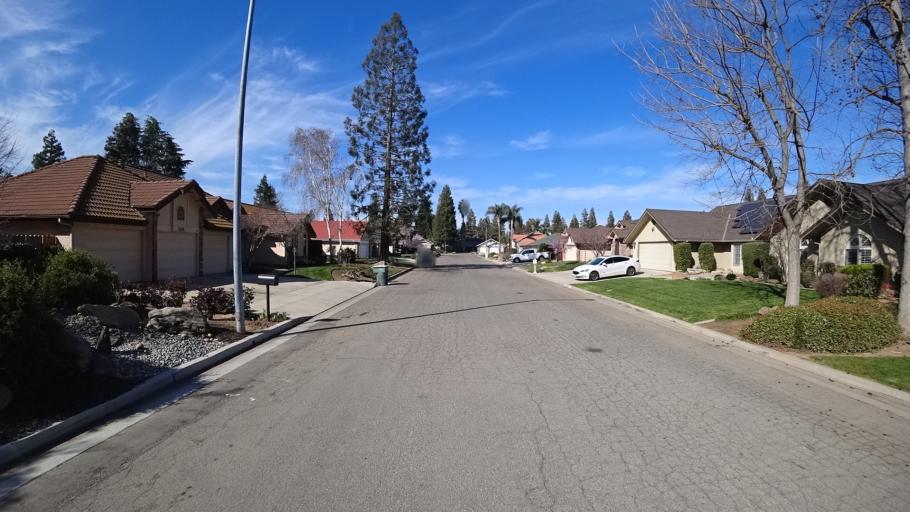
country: US
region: California
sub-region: Fresno County
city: Clovis
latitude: 36.8580
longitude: -119.7548
